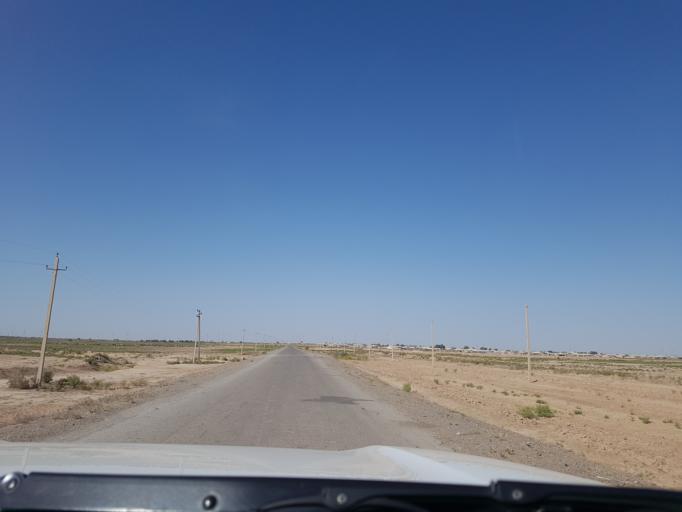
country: IR
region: Razavi Khorasan
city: Sarakhs
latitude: 36.5000
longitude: 61.2536
